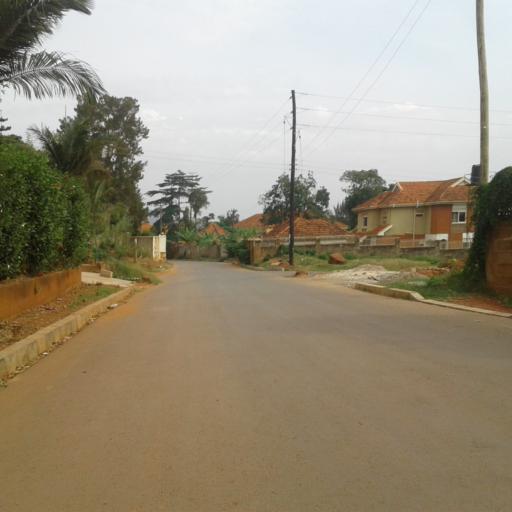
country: UG
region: Central Region
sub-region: Kampala District
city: Kampala
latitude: 0.2739
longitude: 32.6269
